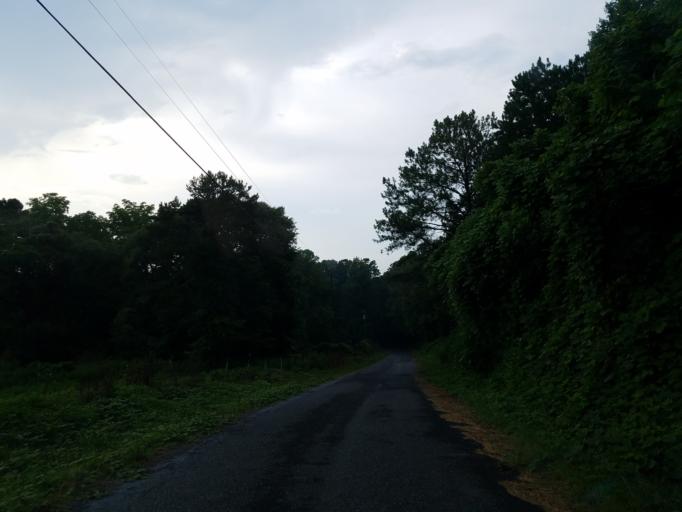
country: US
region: Georgia
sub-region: Pickens County
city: Jasper
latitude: 34.4975
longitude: -84.5315
